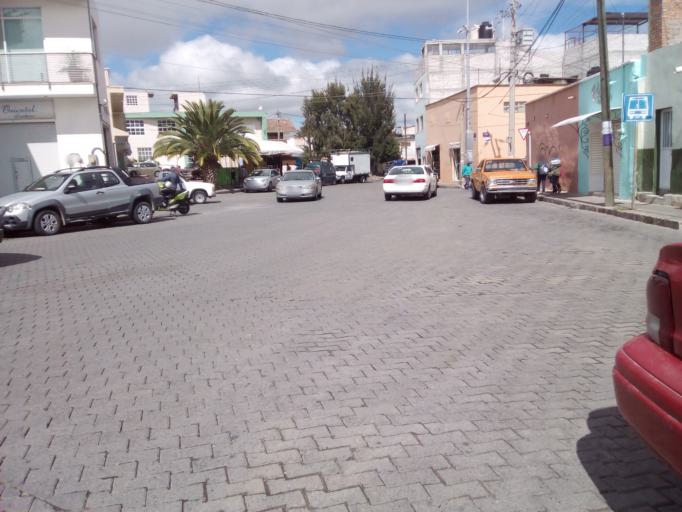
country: MX
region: Guanajuato
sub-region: San Luis de la Paz
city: San Luis de la Paz
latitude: 21.2965
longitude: -100.5131
